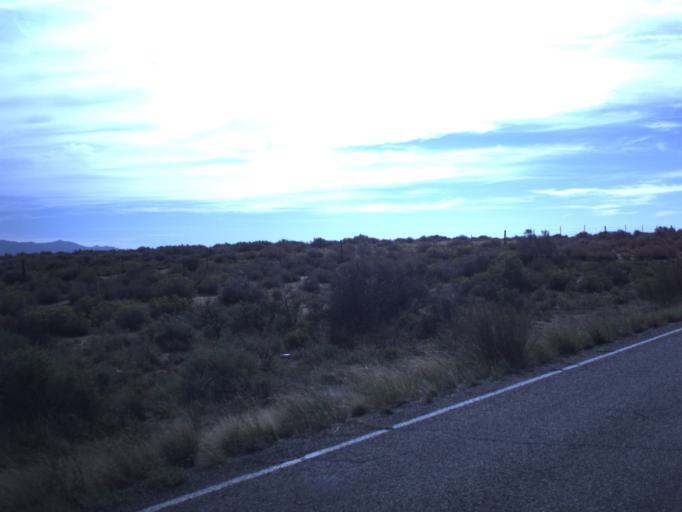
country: US
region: Utah
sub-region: San Juan County
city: Blanding
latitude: 37.3345
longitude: -109.3473
